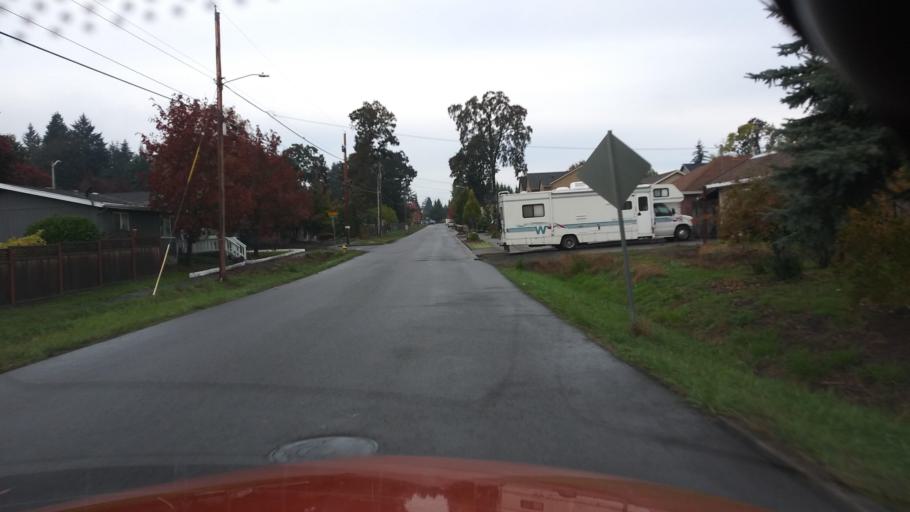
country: US
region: Oregon
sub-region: Washington County
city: North Plains
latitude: 45.5952
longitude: -123.0035
